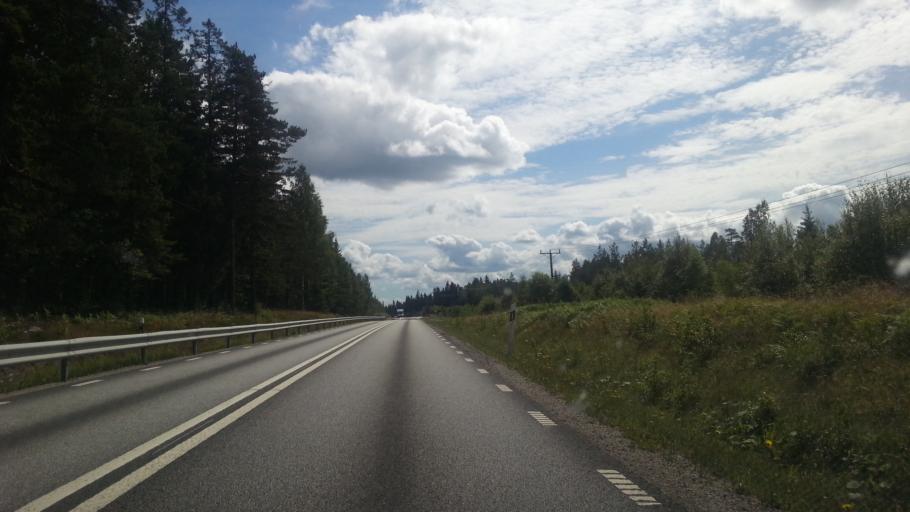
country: SE
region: OErebro
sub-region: Lindesbergs Kommun
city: Stora
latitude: 59.6468
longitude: 15.1306
